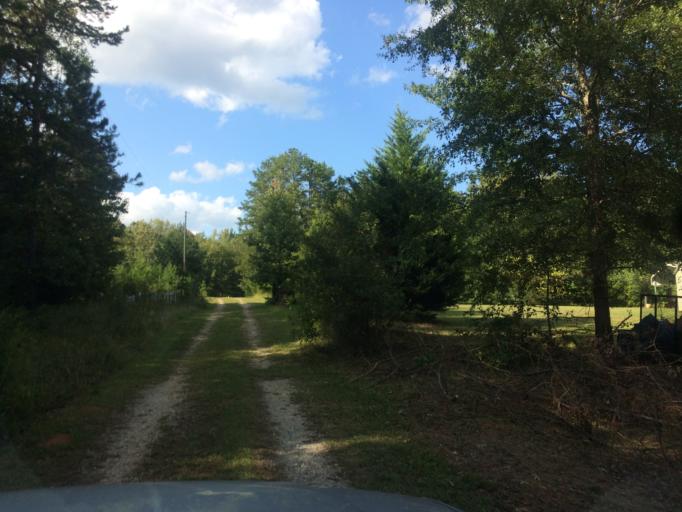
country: US
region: South Carolina
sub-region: Greenwood County
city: Ware Shoals
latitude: 34.4626
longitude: -82.1714
